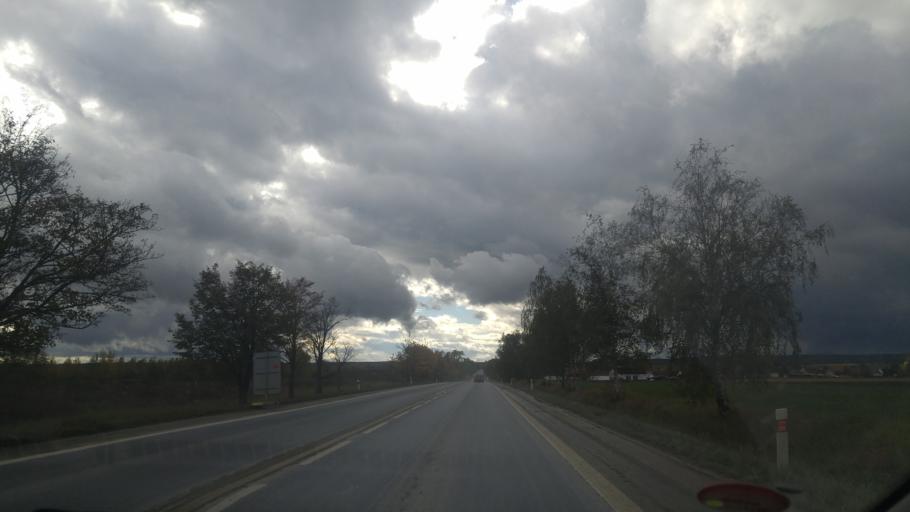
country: CZ
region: Jihocesky
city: Dolni Bukovsko
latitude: 49.1345
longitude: 14.6126
